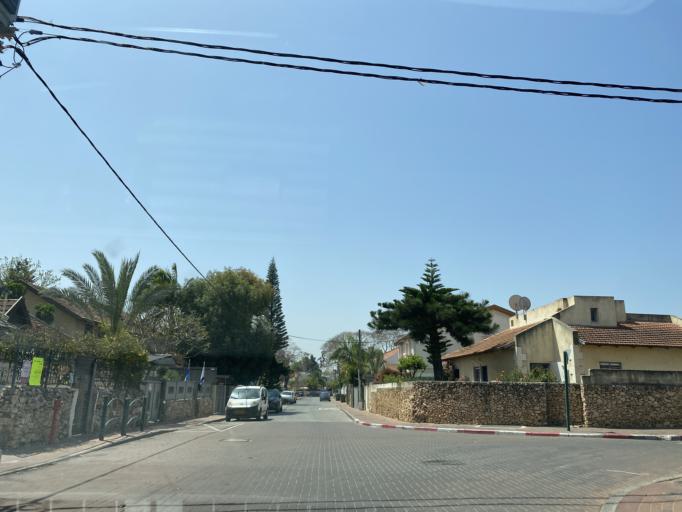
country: IL
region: Central District
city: Ra'anana
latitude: 32.1916
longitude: 34.8687
